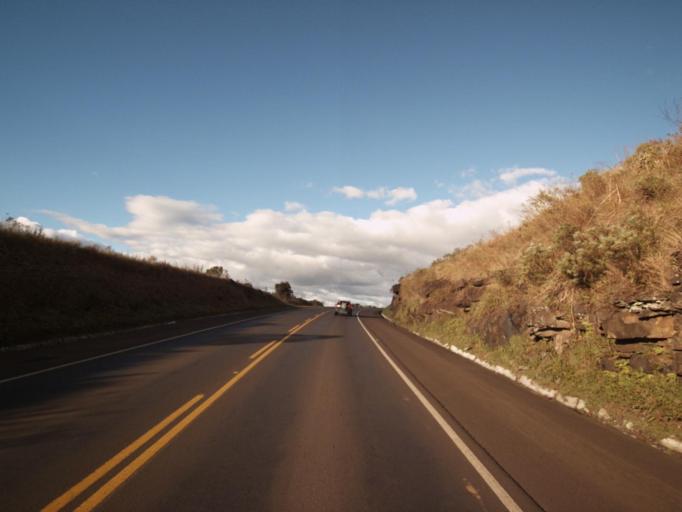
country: BR
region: Santa Catarina
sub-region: Campos Novos
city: Campos Novos
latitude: -27.3590
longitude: -51.3240
